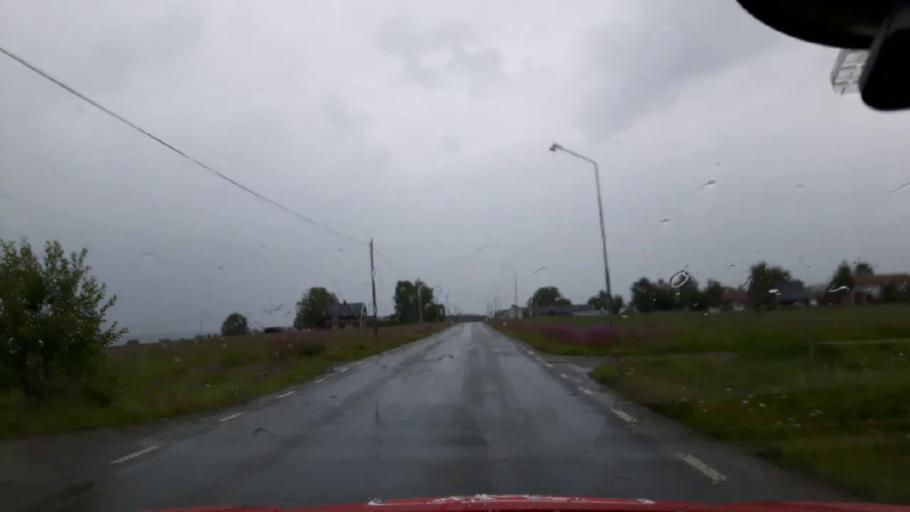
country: SE
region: Jaemtland
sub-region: OEstersunds Kommun
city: Brunflo
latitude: 62.9883
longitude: 14.8069
